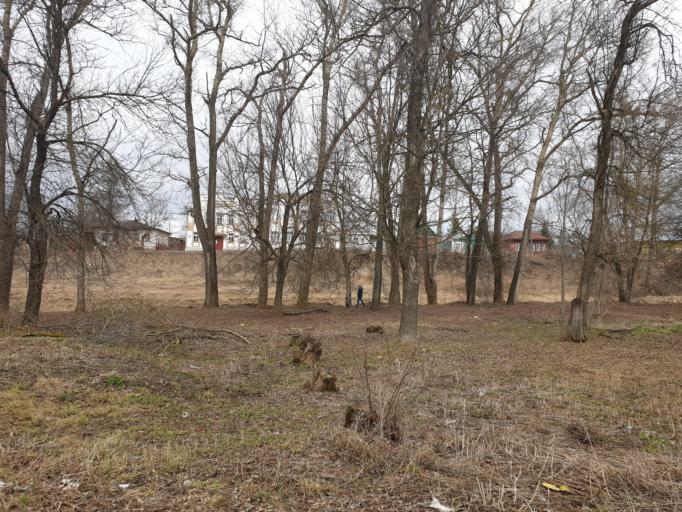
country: RU
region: Kostroma
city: Nerekhta
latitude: 57.4610
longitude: 40.5736
